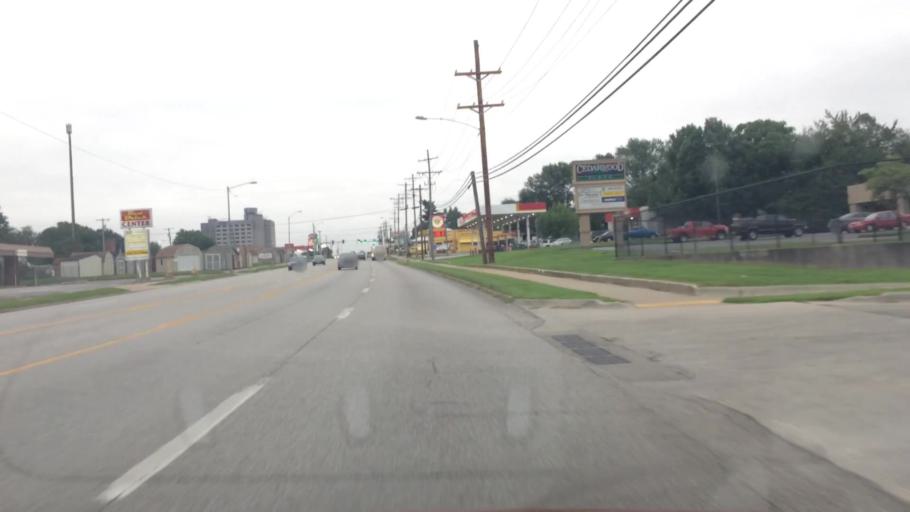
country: US
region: Missouri
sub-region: Greene County
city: Springfield
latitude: 37.2402
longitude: -93.2692
